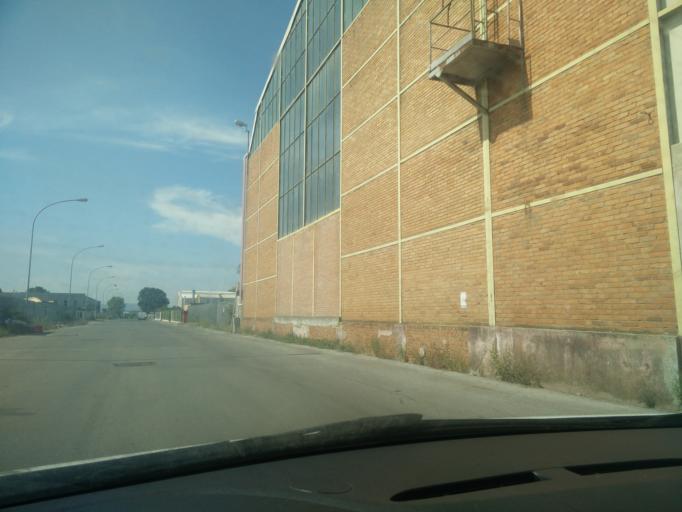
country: IT
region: Tuscany
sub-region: Provincia di Massa-Carrara
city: Massa
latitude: 44.0278
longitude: 10.1002
